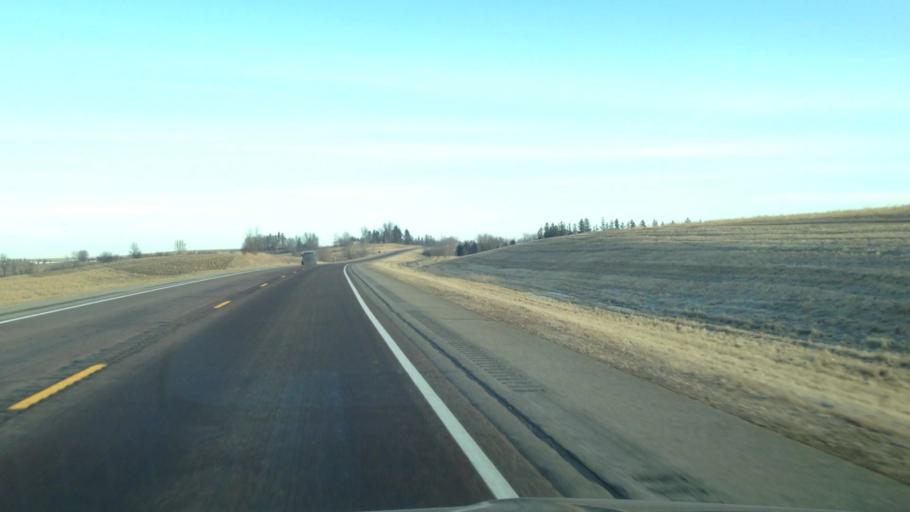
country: US
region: Minnesota
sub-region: Goodhue County
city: Zumbrota
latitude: 44.3135
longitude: -92.6615
